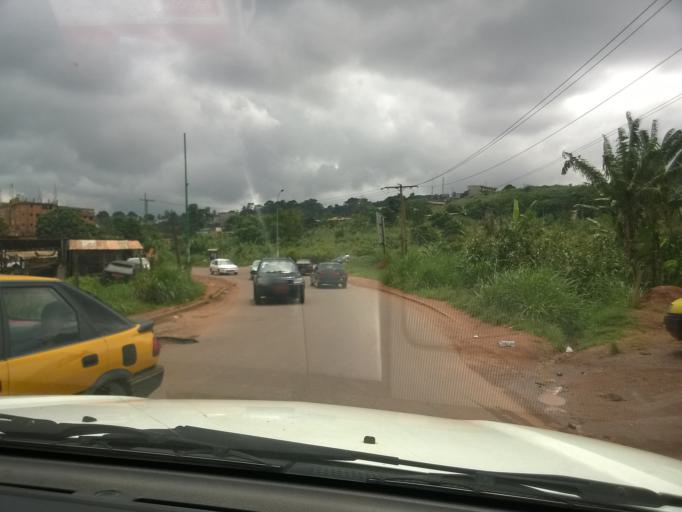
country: CM
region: Centre
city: Yaounde
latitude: 3.8479
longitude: 11.5022
